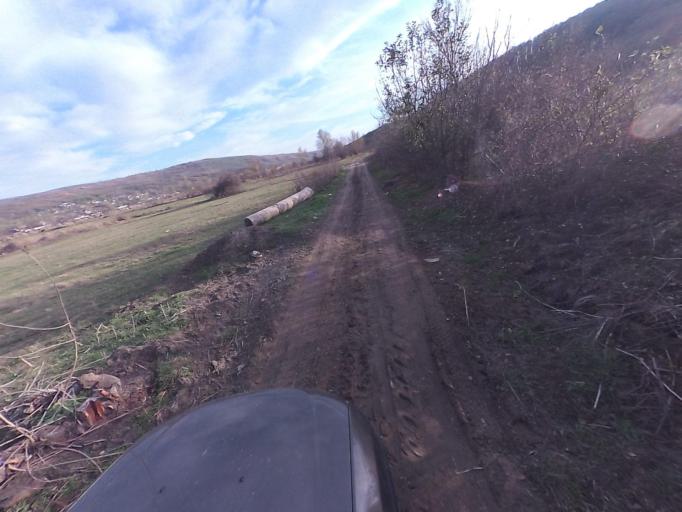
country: RO
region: Vaslui
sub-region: Comuna Gherghesti
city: Gherghesti
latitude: 46.4881
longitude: 27.5298
